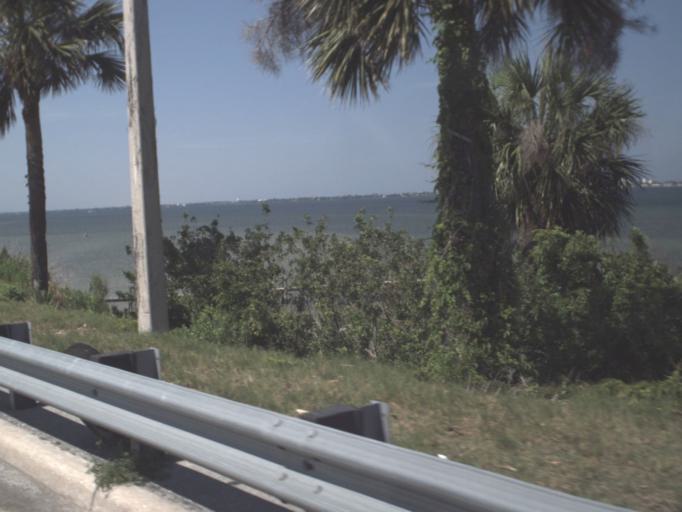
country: US
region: Florida
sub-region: Brevard County
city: Melbourne
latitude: 28.0894
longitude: -80.6078
